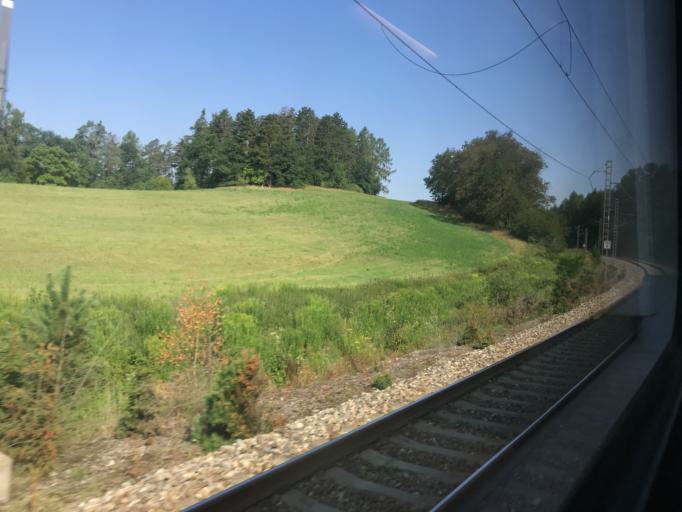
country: CZ
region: Central Bohemia
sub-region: Okres Praha-Vychod
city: Mnichovice
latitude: 49.9031
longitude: 14.7280
